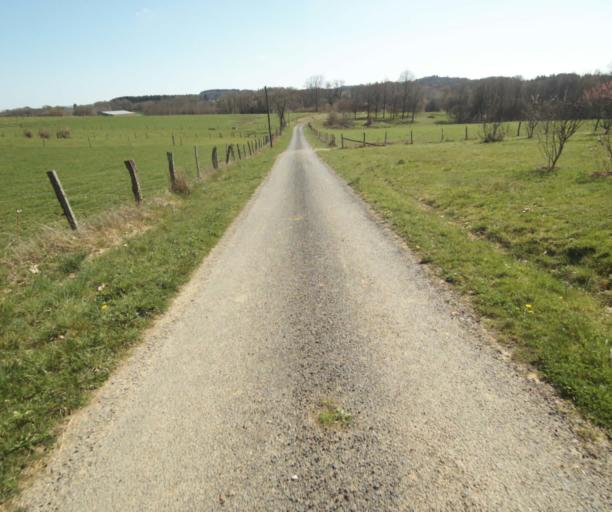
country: FR
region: Limousin
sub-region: Departement de la Correze
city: Saint-Mexant
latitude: 45.2904
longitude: 1.6824
